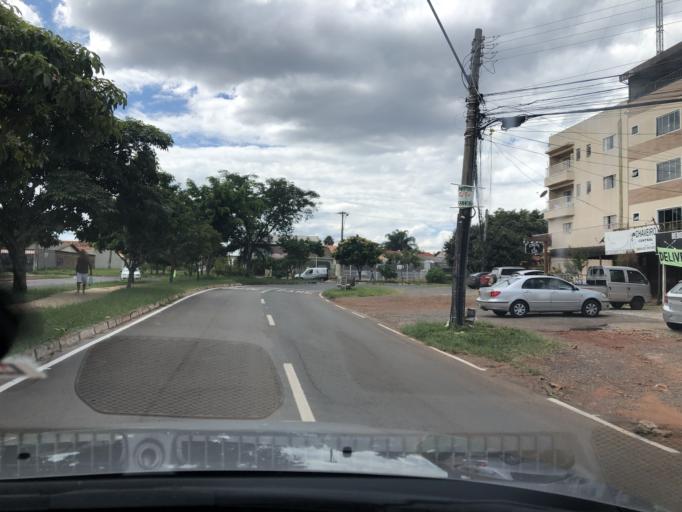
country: BR
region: Federal District
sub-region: Brasilia
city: Brasilia
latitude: -15.9939
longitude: -47.9955
